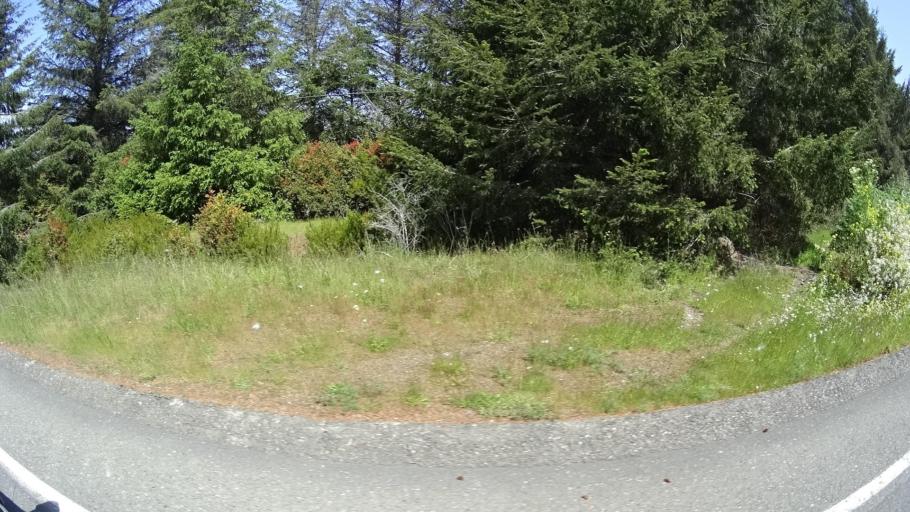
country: US
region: California
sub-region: Humboldt County
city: Fortuna
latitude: 40.6422
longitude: -124.2113
